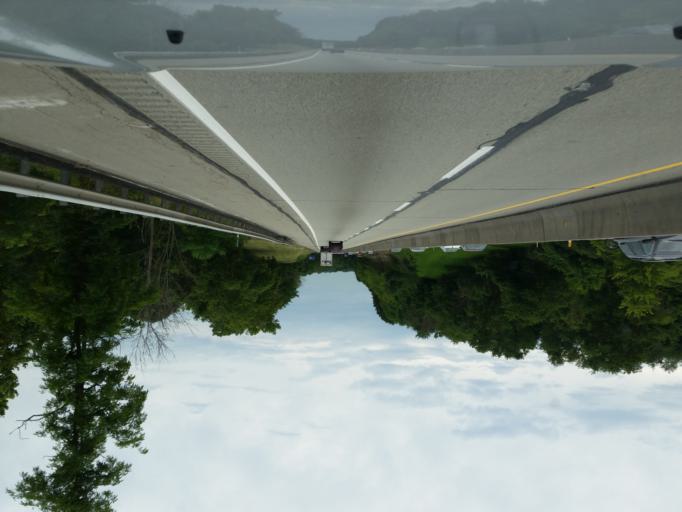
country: US
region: Pennsylvania
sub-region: Westmoreland County
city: Manor
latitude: 40.3492
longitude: -79.6870
